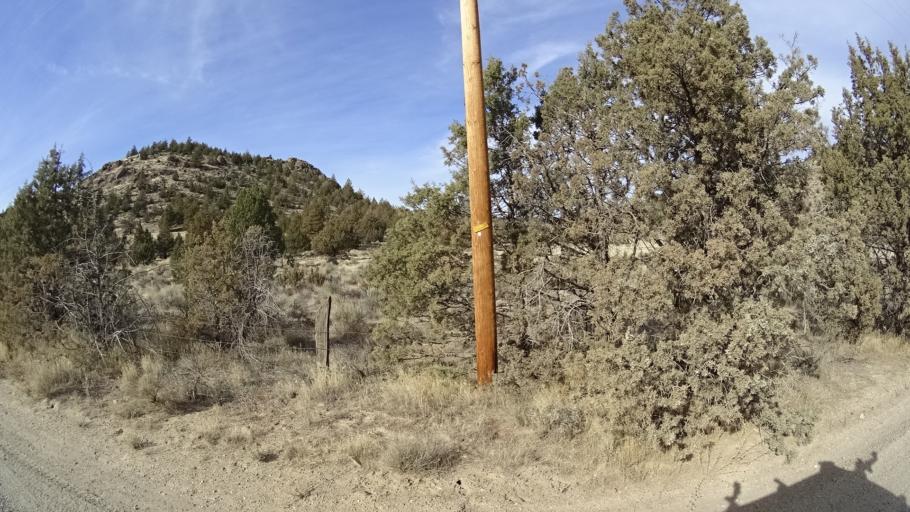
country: US
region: California
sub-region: Siskiyou County
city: Montague
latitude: 41.5801
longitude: -122.4569
